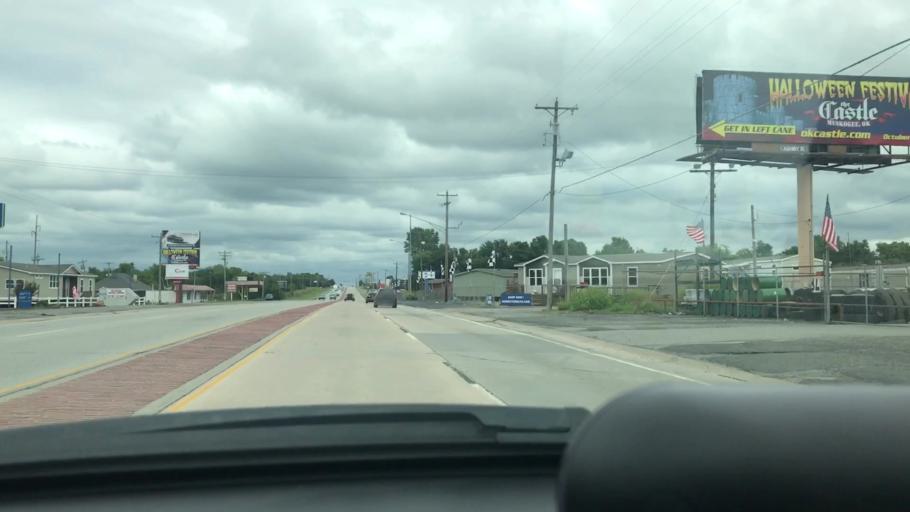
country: US
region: Oklahoma
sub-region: Muskogee County
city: Muskogee
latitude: 35.7746
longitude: -95.4025
